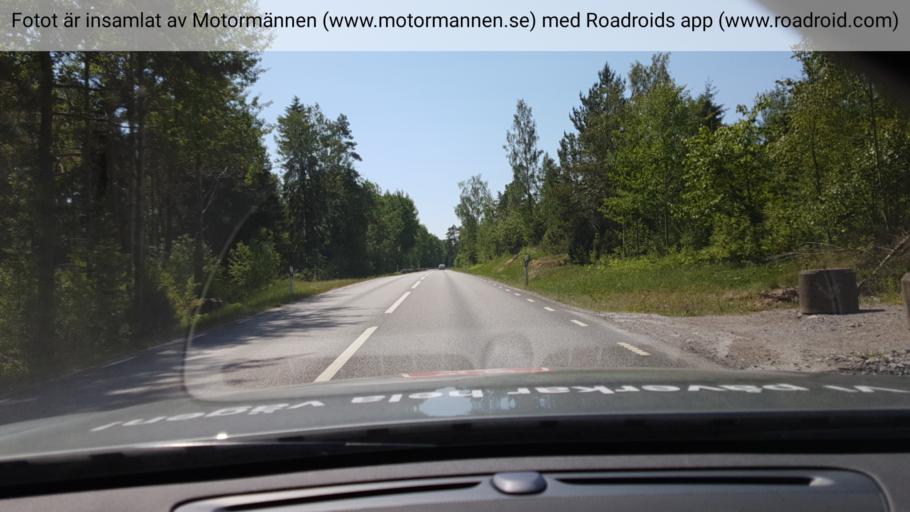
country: SE
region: Stockholm
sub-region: Norrtalje Kommun
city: Rimbo
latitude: 59.6687
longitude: 18.3507
